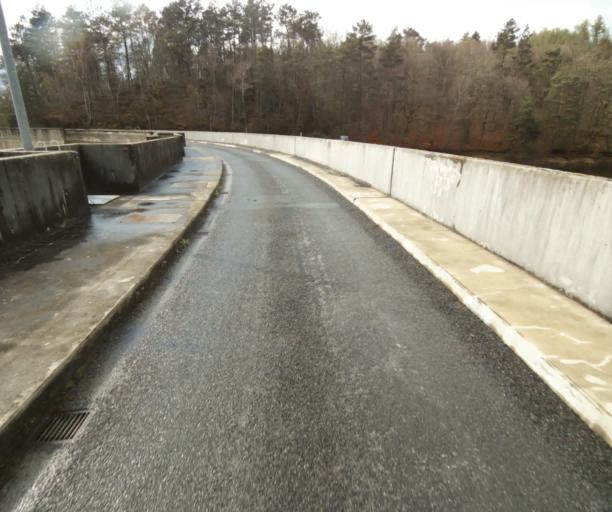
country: FR
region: Limousin
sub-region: Departement de la Correze
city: Saint-Privat
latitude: 45.2478
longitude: 1.9968
